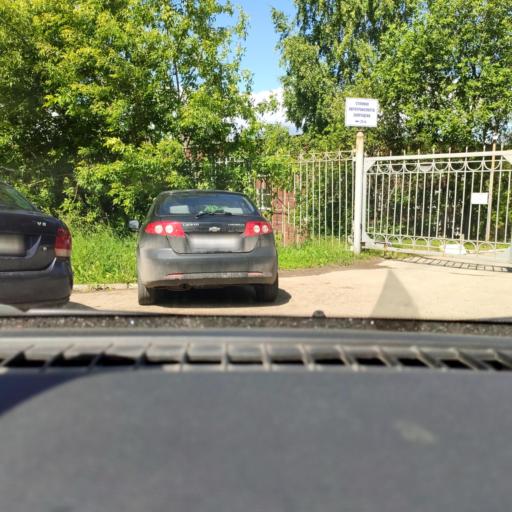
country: RU
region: Perm
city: Perm
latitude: 57.9734
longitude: 56.2227
